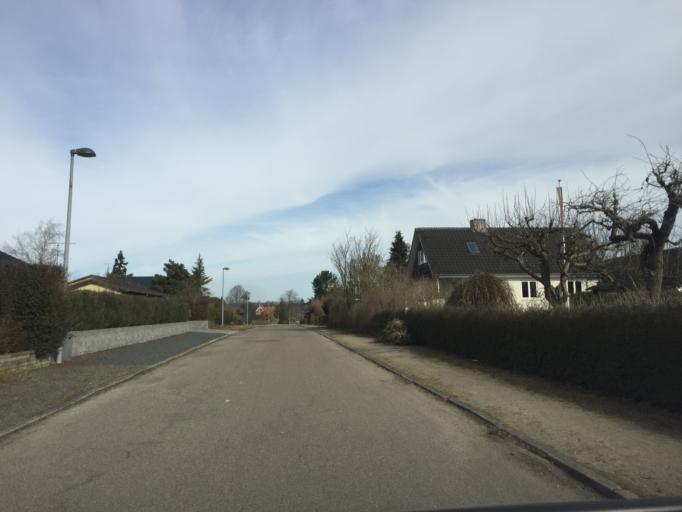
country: DK
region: Capital Region
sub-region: Fureso Kommune
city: Farum
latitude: 55.8117
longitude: 12.3636
